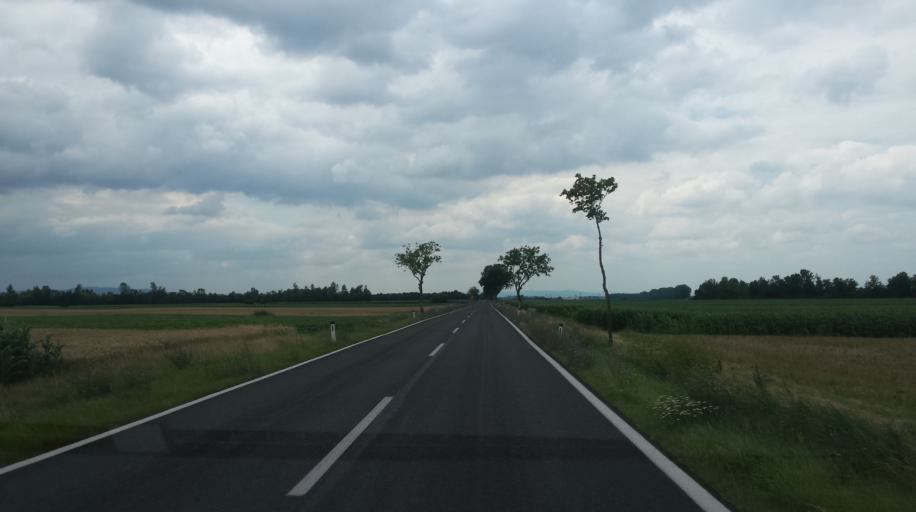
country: AT
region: Lower Austria
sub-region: Politischer Bezirk Wien-Umgebung
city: Moosbrunn
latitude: 48.0027
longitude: 16.4455
